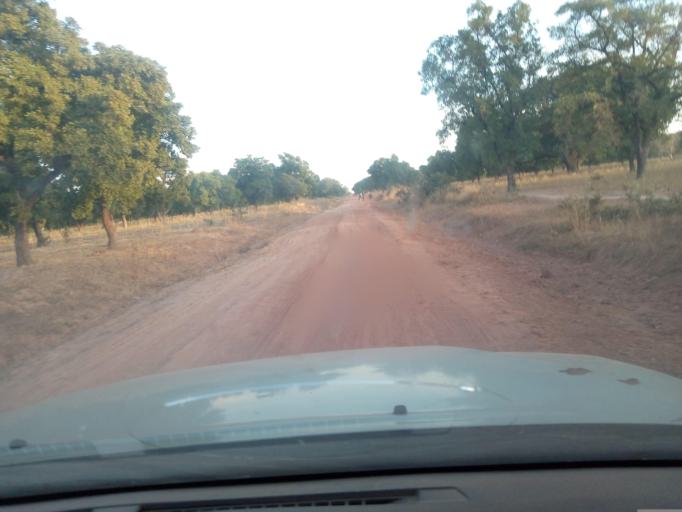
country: ML
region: Koulikoro
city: Dioila
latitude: 12.2095
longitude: -6.2002
